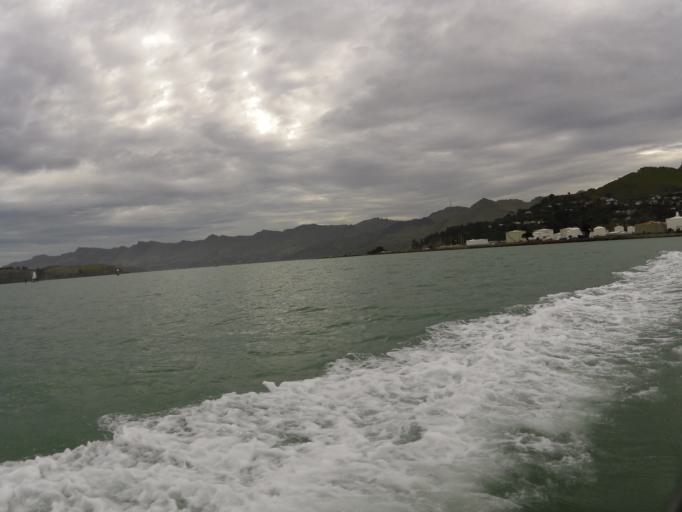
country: NZ
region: Canterbury
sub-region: Christchurch City
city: Christchurch
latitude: -43.6091
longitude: 172.7182
